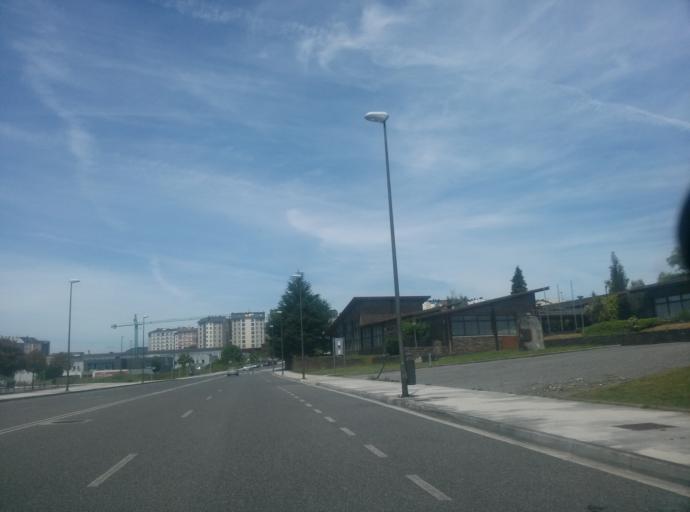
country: ES
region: Galicia
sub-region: Provincia de Lugo
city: Lugo
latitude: 42.9979
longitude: -7.5423
